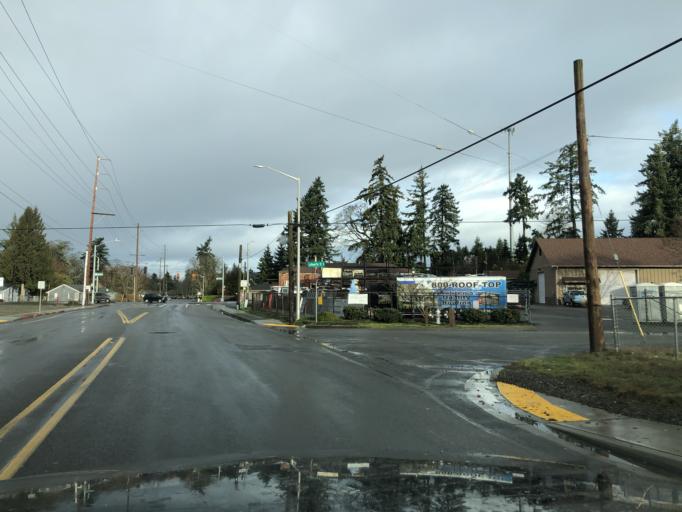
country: US
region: Washington
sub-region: Pierce County
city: Parkland
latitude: 47.1546
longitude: -122.4372
